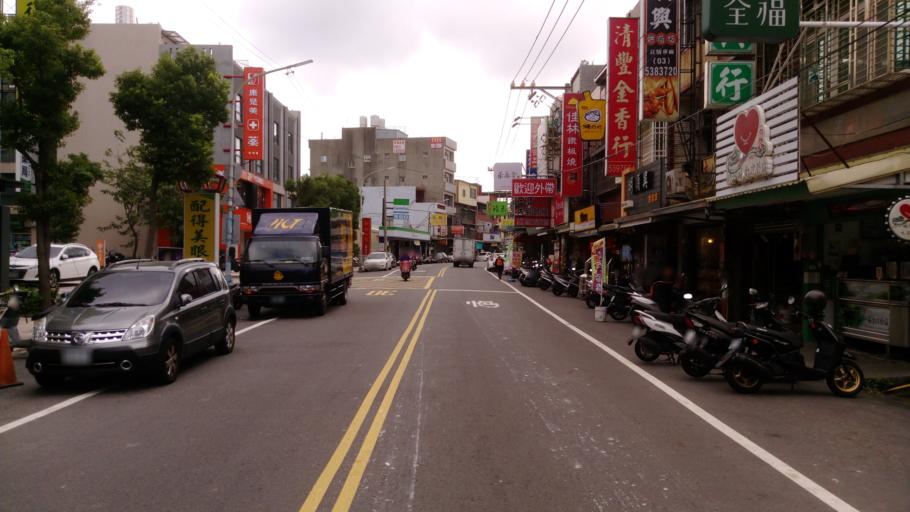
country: TW
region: Taiwan
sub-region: Hsinchu
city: Hsinchu
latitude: 24.7896
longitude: 120.9278
